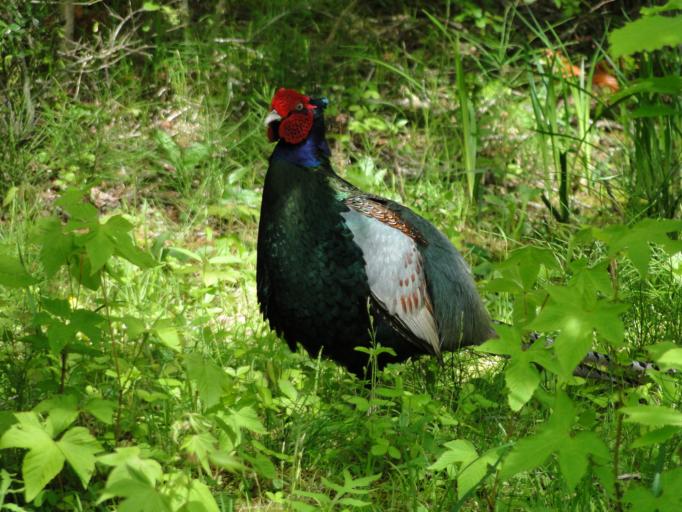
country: JP
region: Shizuoka
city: Gotemba
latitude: 35.2660
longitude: 139.0070
